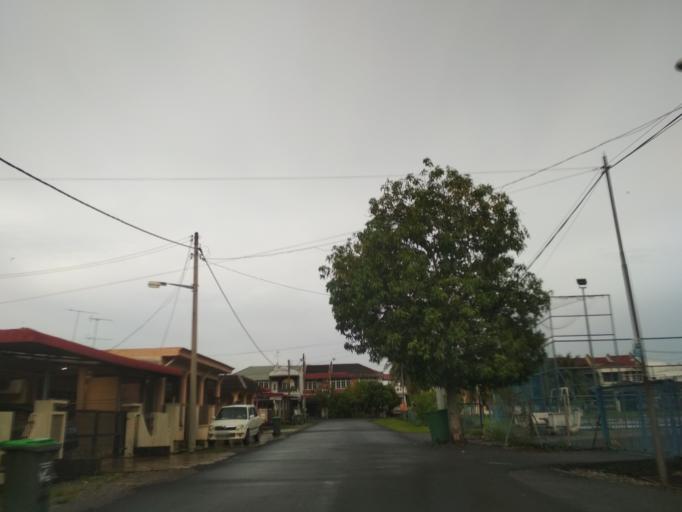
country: MY
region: Perlis
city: Kangar
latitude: 6.4486
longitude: 100.2060
